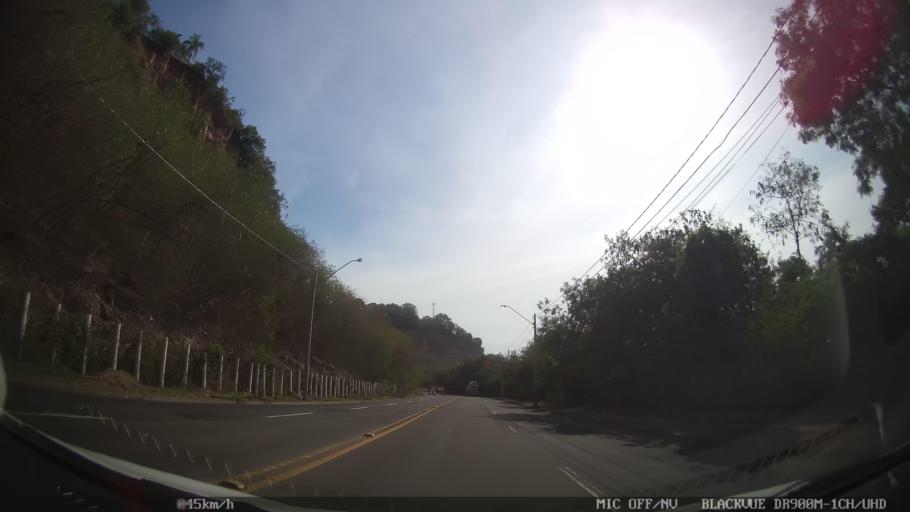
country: BR
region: Sao Paulo
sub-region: Piracicaba
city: Piracicaba
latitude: -22.7170
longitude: -47.6775
